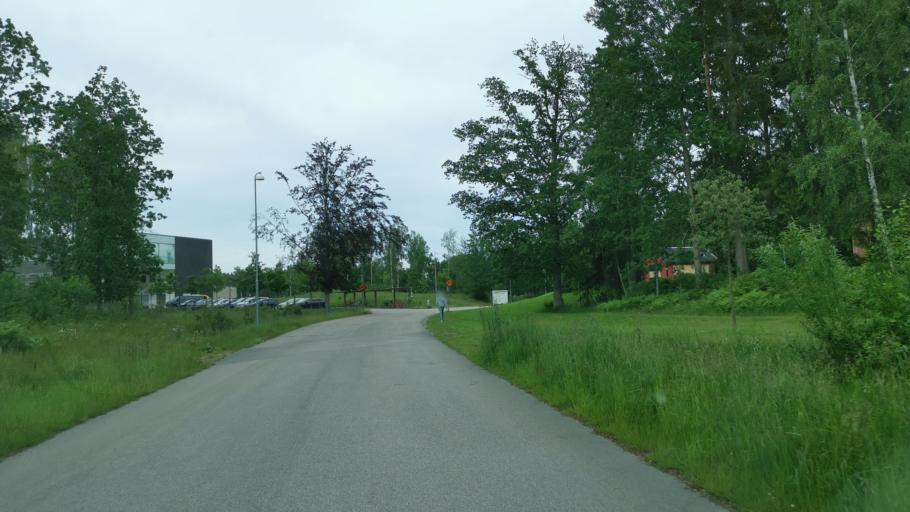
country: SE
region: Vaestra Goetaland
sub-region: Vanersborgs Kommun
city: Vargon
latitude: 58.3438
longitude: 12.3607
